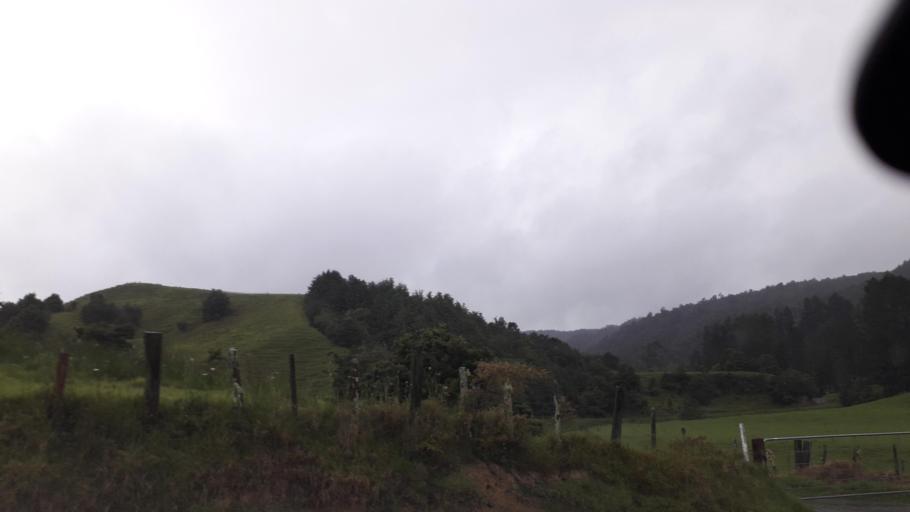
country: NZ
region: Northland
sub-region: Far North District
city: Waimate North
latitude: -35.1611
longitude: 173.7201
